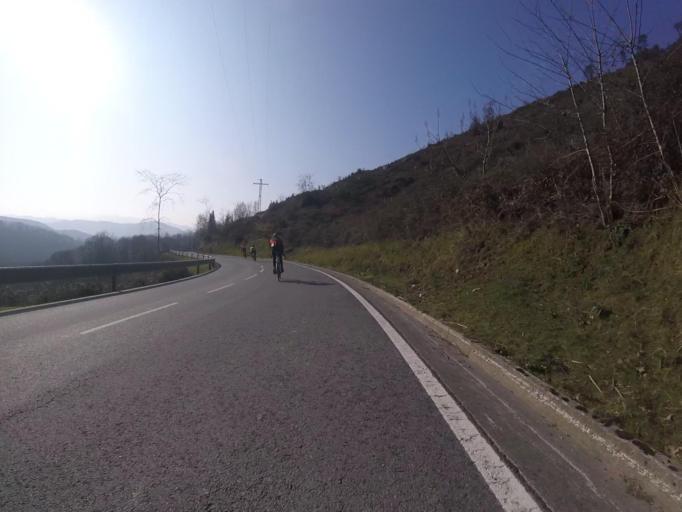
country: ES
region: Navarre
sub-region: Provincia de Navarra
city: Bera
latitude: 43.3036
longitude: -1.6897
